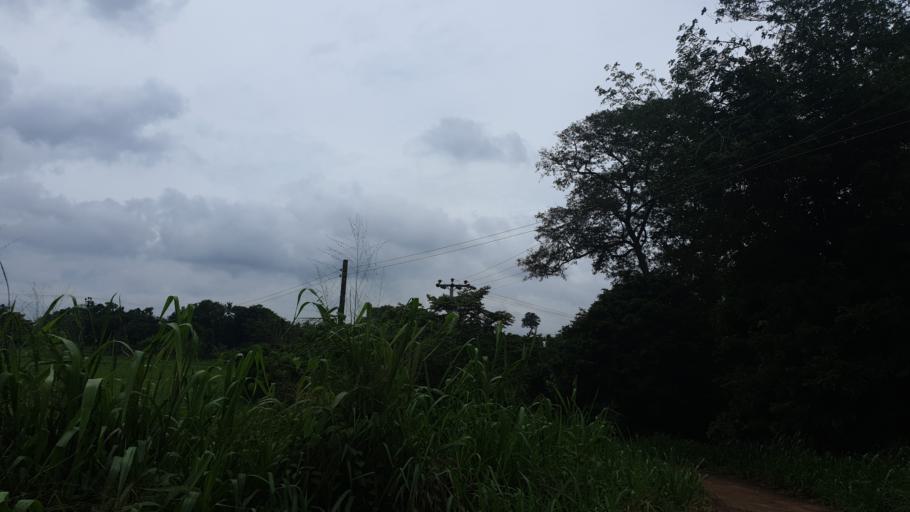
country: LK
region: Western
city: Gampaha
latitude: 7.0955
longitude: 79.9933
